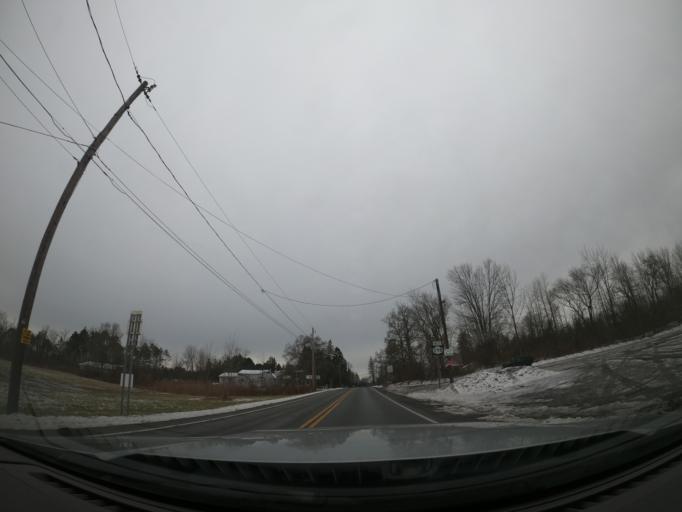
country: US
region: New York
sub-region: Onondaga County
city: Minoa
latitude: 43.1153
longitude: -76.0038
